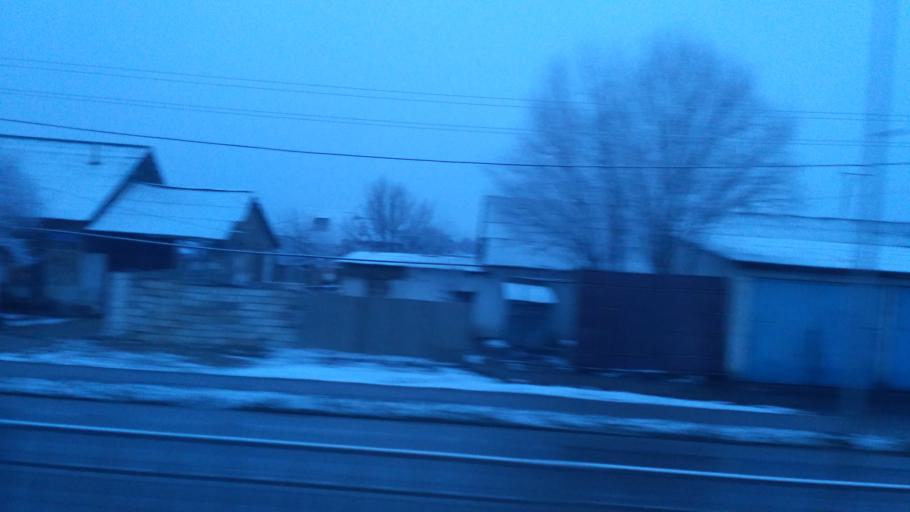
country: KZ
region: Ongtustik Qazaqstan
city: Shymkent
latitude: 42.3755
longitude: 69.5003
